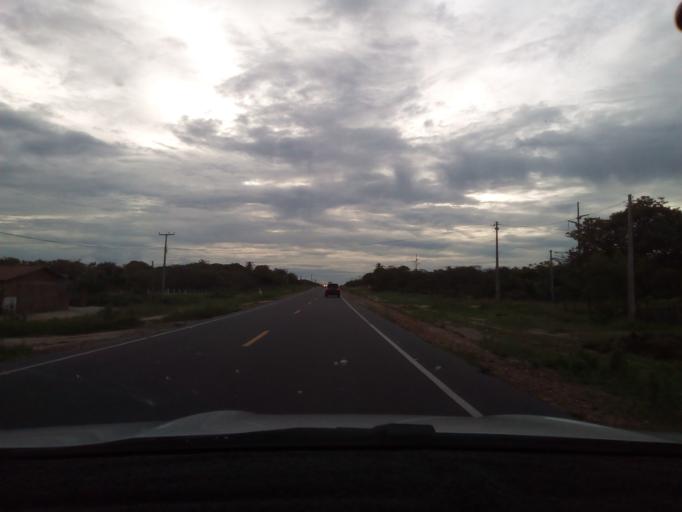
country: BR
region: Ceara
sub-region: Aracati
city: Aracati
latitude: -4.3692
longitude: -37.9414
